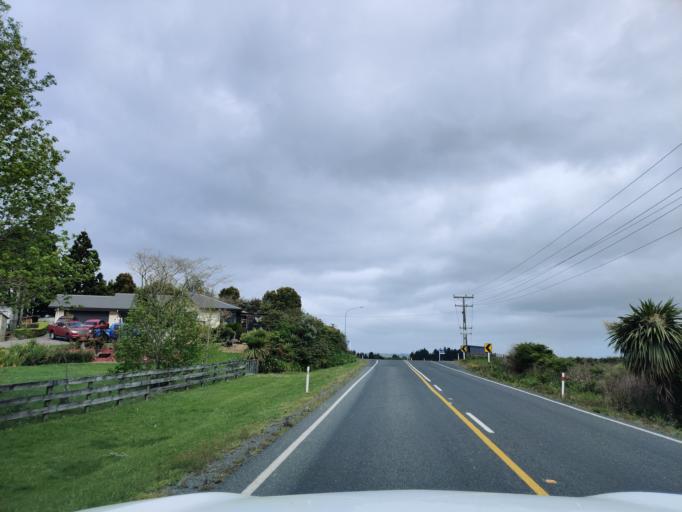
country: NZ
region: Waikato
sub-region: Waikato District
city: Ngaruawahia
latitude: -37.5777
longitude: 175.1352
